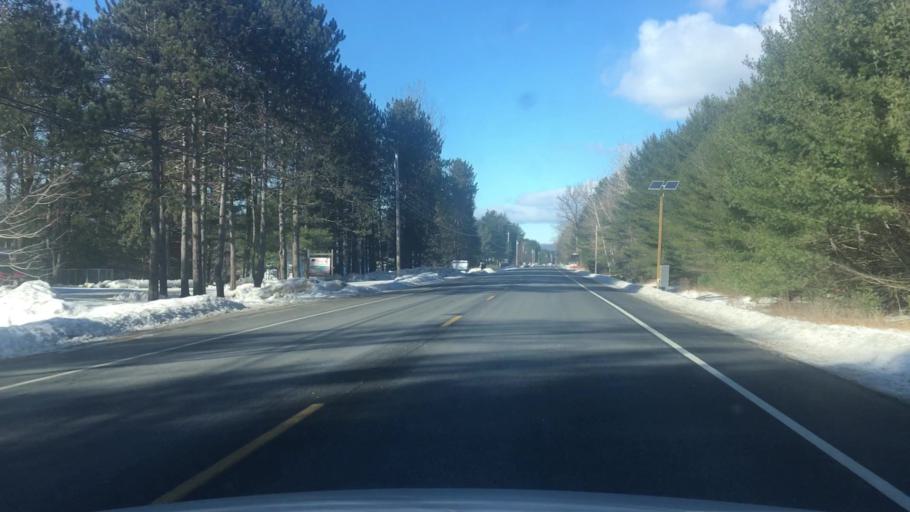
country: US
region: Maine
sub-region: Somerset County
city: Madison
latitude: 44.9390
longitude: -69.8431
